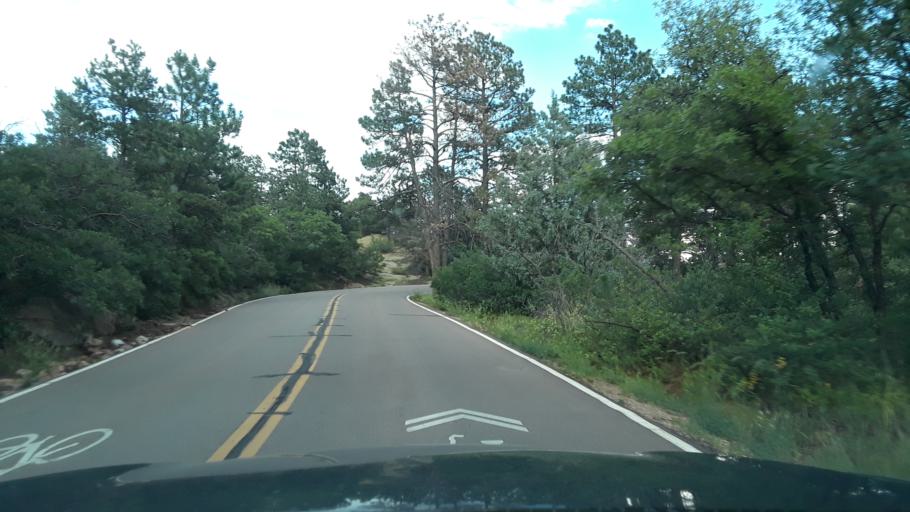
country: US
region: Colorado
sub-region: El Paso County
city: Colorado Springs
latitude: 38.8791
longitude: -104.7696
